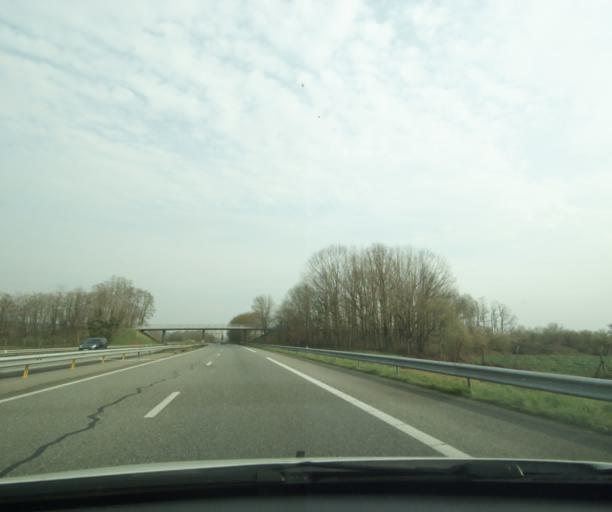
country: FR
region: Aquitaine
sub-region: Departement des Pyrenees-Atlantiques
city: Artix
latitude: 43.3867
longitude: -0.5321
